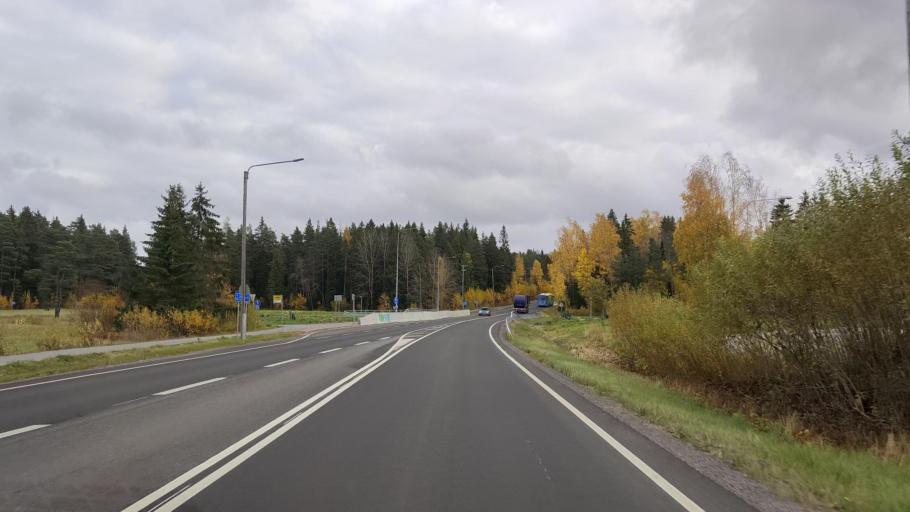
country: FI
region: Varsinais-Suomi
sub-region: Turku
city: Kaarina
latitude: 60.4611
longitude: 22.3594
